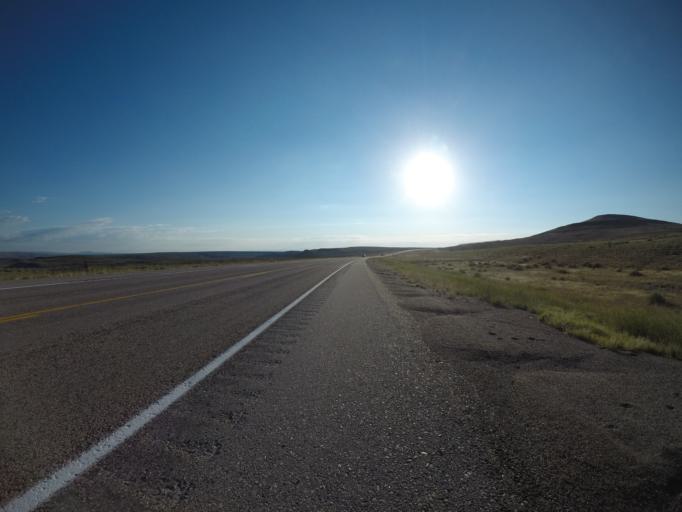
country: US
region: Wyoming
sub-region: Lincoln County
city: Kemmerer
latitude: 41.8892
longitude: -110.4175
